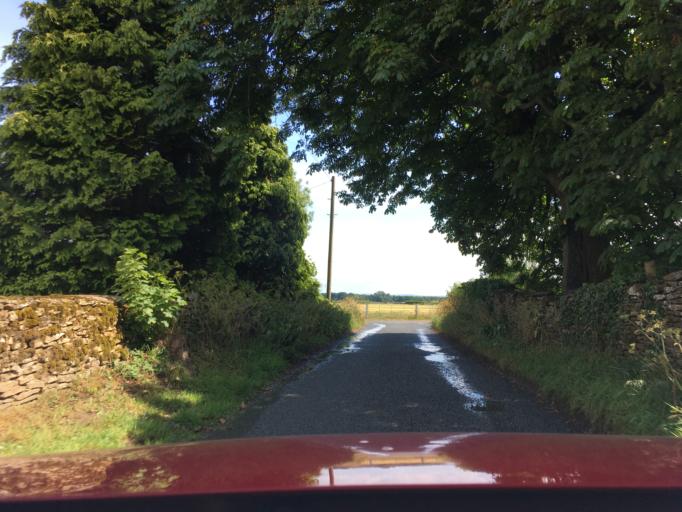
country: GB
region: England
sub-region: Wiltshire
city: Luckington
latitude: 51.6176
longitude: -2.2518
